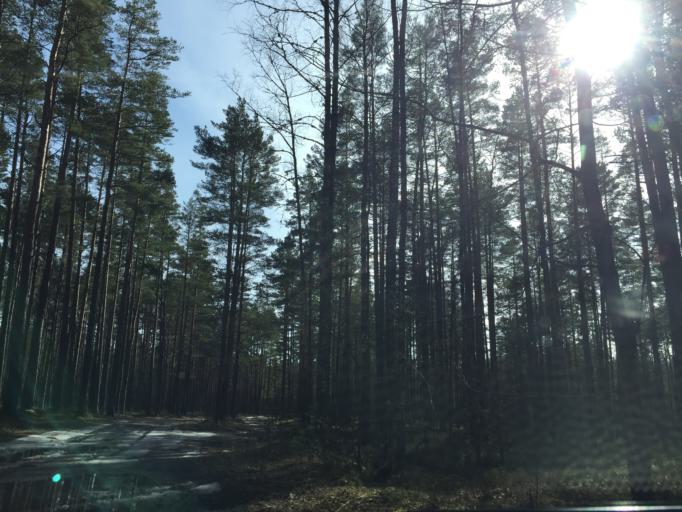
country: EE
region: Paernumaa
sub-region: Paernu linn
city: Parnu
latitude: 58.2400
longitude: 24.5215
